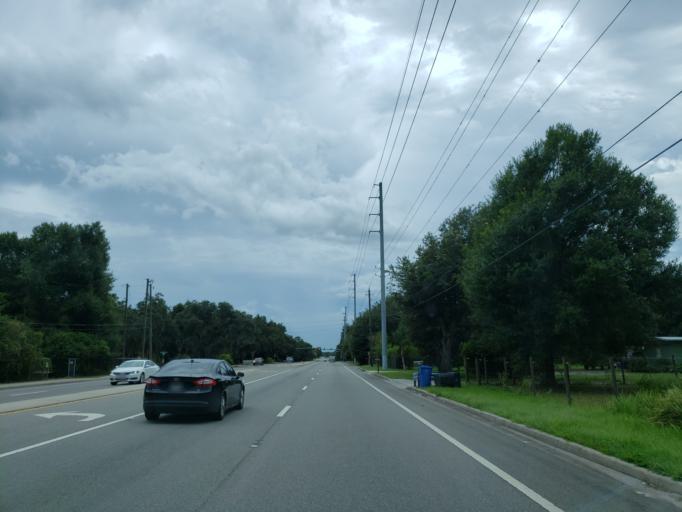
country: US
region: Florida
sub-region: Polk County
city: Willow Oak
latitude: 27.9407
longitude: -82.0554
